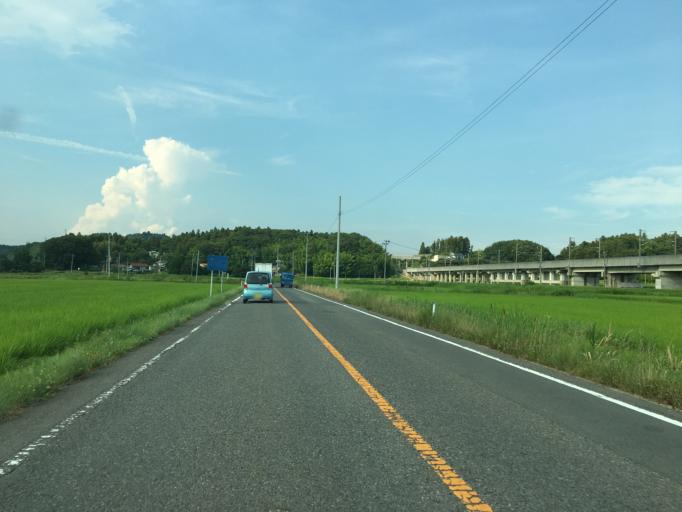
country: JP
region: Fukushima
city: Motomiya
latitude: 37.4750
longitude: 140.4143
